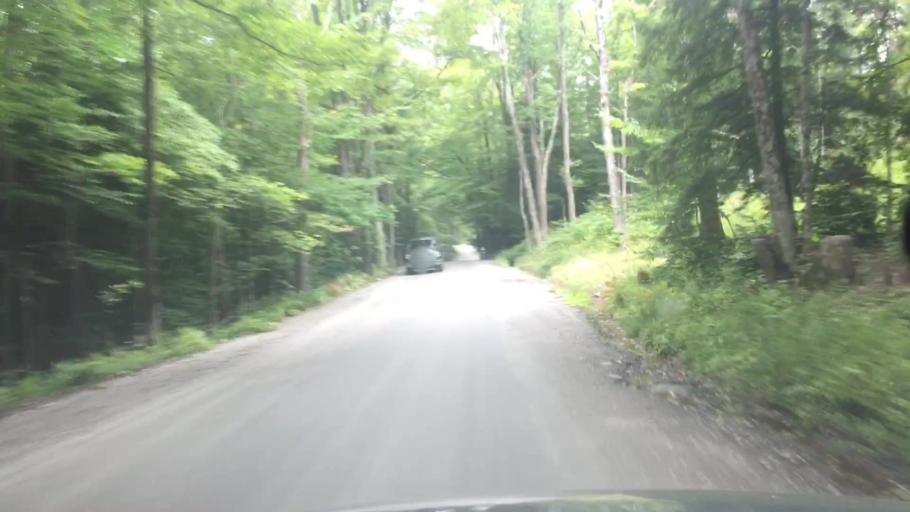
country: US
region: Vermont
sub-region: Windham County
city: Dover
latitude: 42.8214
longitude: -72.7751
